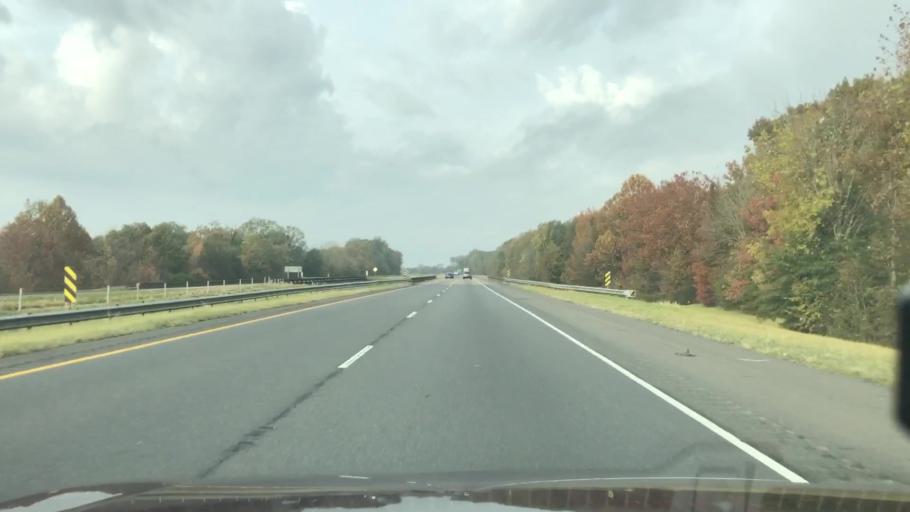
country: US
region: Louisiana
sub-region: Richland Parish
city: Delhi
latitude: 32.4549
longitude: -91.6057
